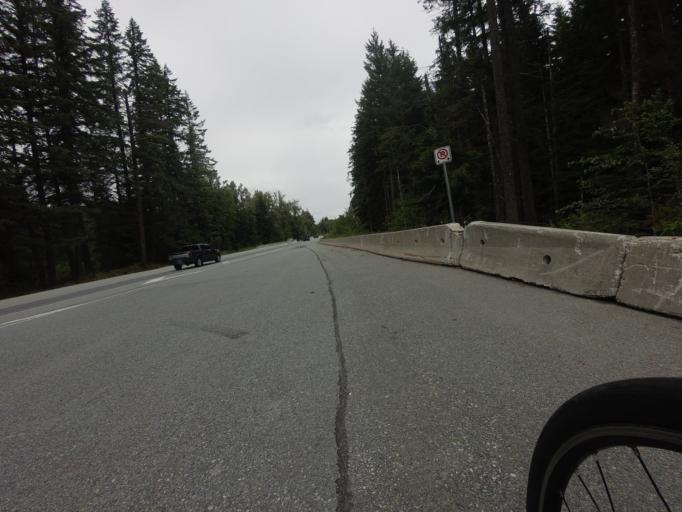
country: CA
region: British Columbia
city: Whistler
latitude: 49.9515
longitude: -123.1622
